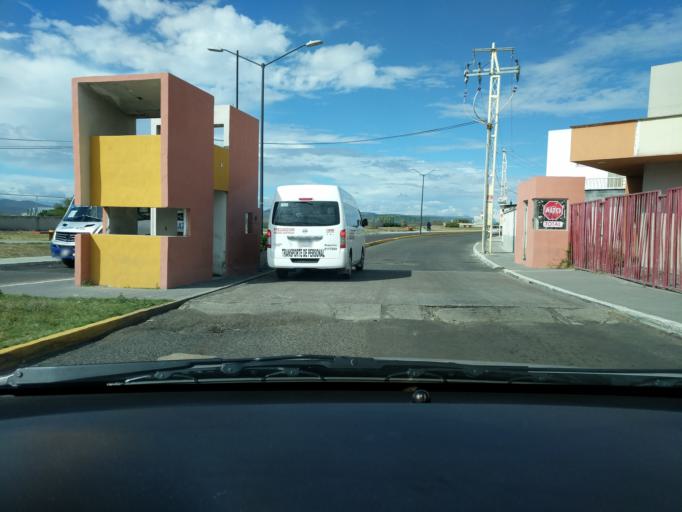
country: MX
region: Queretaro
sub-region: El Marques
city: Paseos del Marques
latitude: 20.6025
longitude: -100.2461
